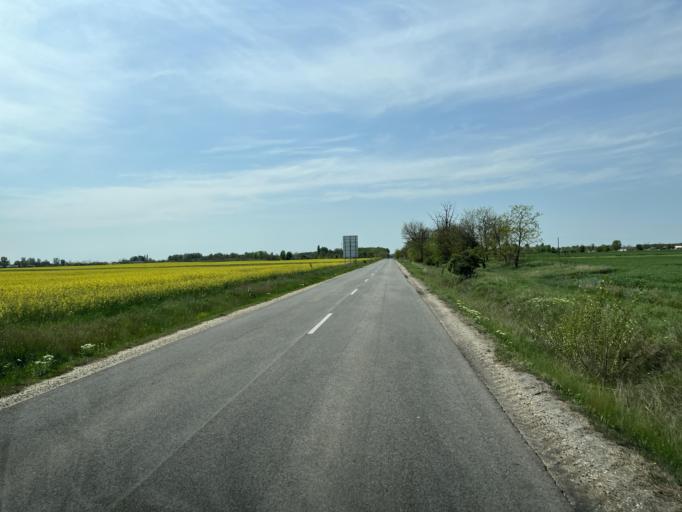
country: HU
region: Pest
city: Abony
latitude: 47.2165
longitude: 20.0159
